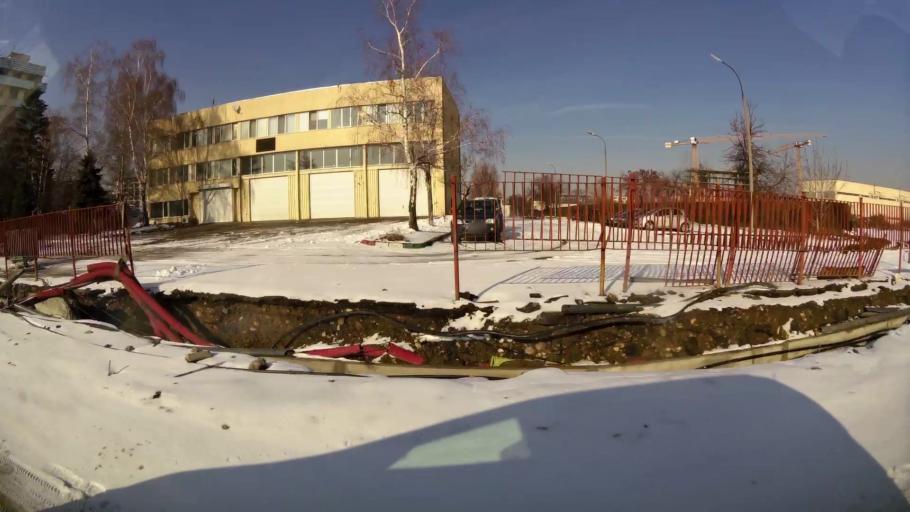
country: BG
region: Sofia-Capital
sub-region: Stolichna Obshtina
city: Sofia
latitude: 42.6569
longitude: 23.3191
